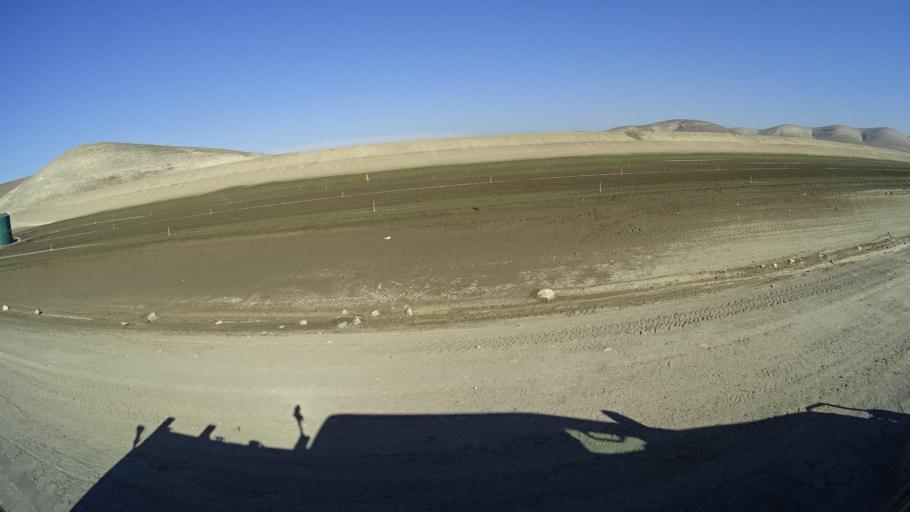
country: US
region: California
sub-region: Monterey County
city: King City
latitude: 36.1934
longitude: -121.0356
